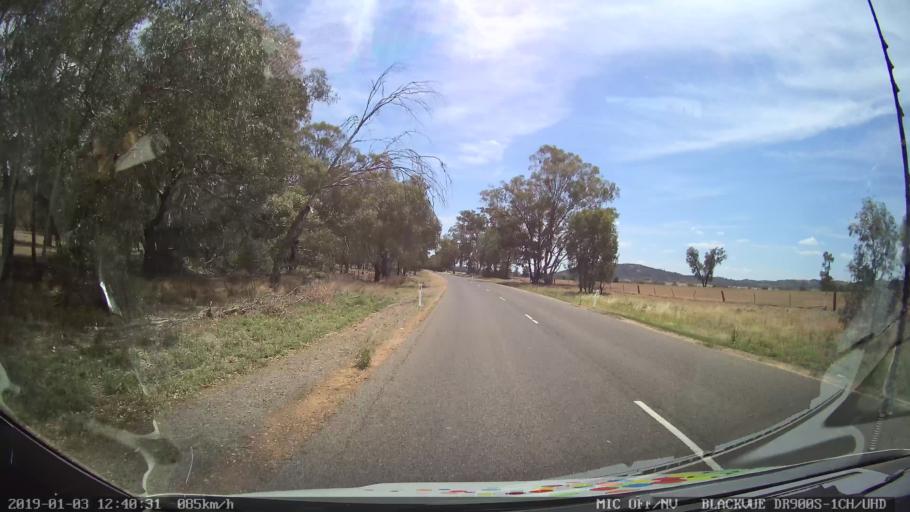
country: AU
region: New South Wales
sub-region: Weddin
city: Grenfell
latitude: -33.8115
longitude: 148.2128
